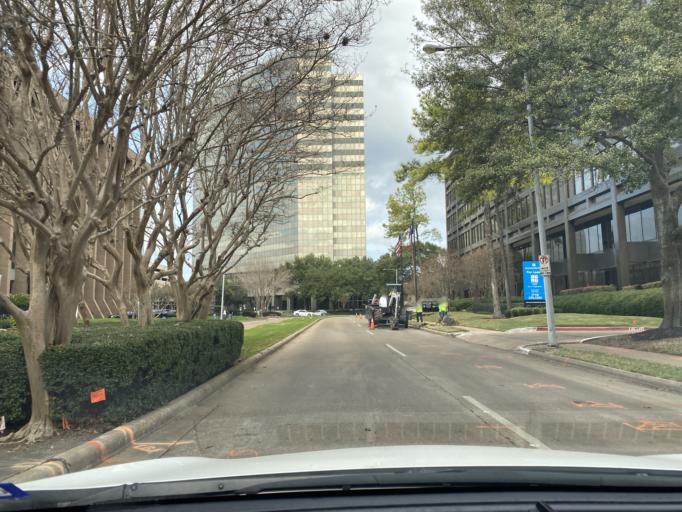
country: US
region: Texas
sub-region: Harris County
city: Hunters Creek Village
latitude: 29.7479
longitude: -95.4731
